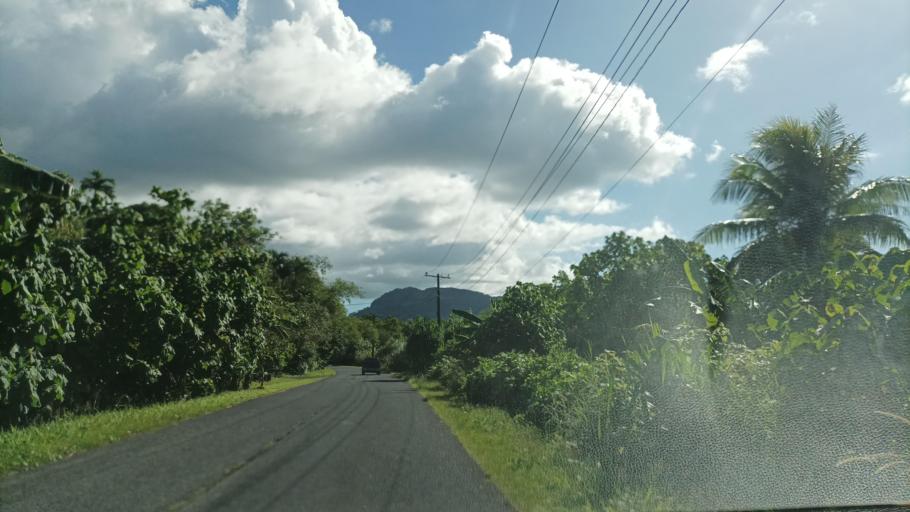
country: FM
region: Pohnpei
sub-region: Kolonia Municipality
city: Kolonia
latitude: 6.9691
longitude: 158.2530
